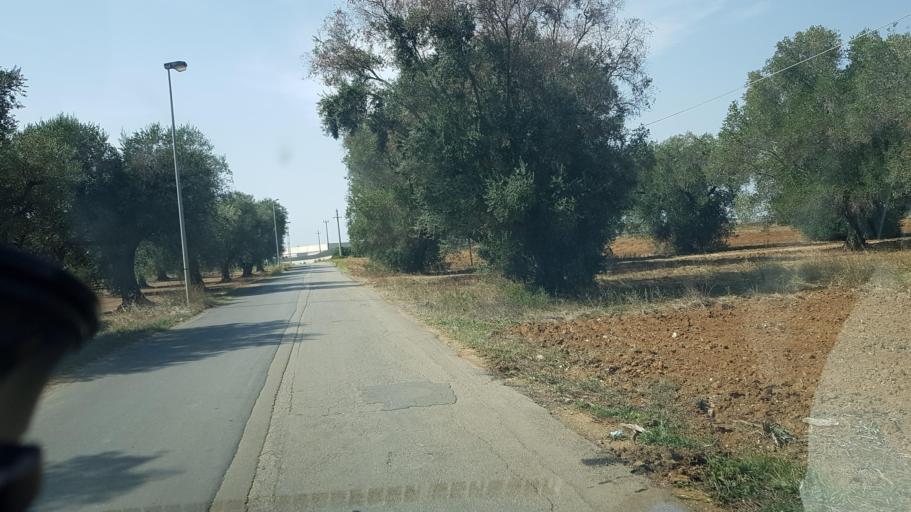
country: IT
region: Apulia
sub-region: Provincia di Brindisi
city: Mesagne
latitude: 40.5694
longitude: 17.8305
